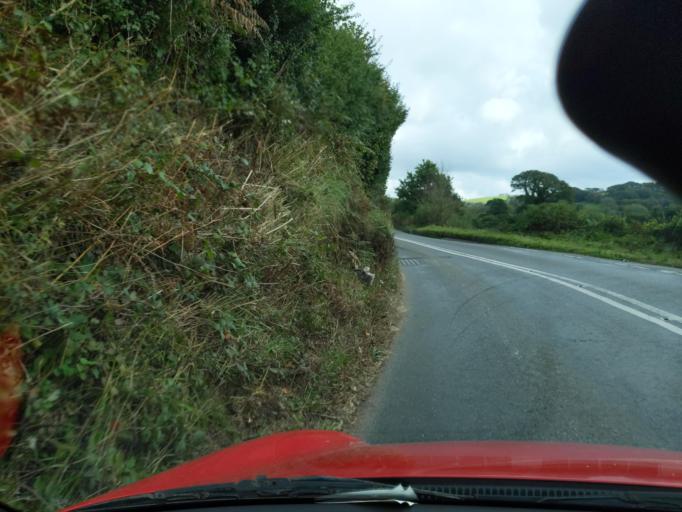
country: GB
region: England
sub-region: Devon
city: Modbury
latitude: 50.3451
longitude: -3.8854
